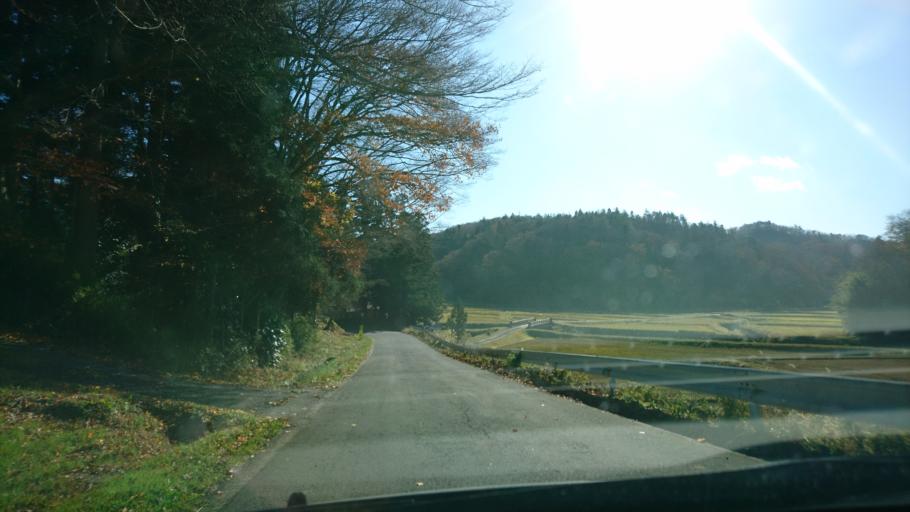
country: JP
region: Iwate
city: Ichinoseki
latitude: 38.9997
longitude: 141.0857
